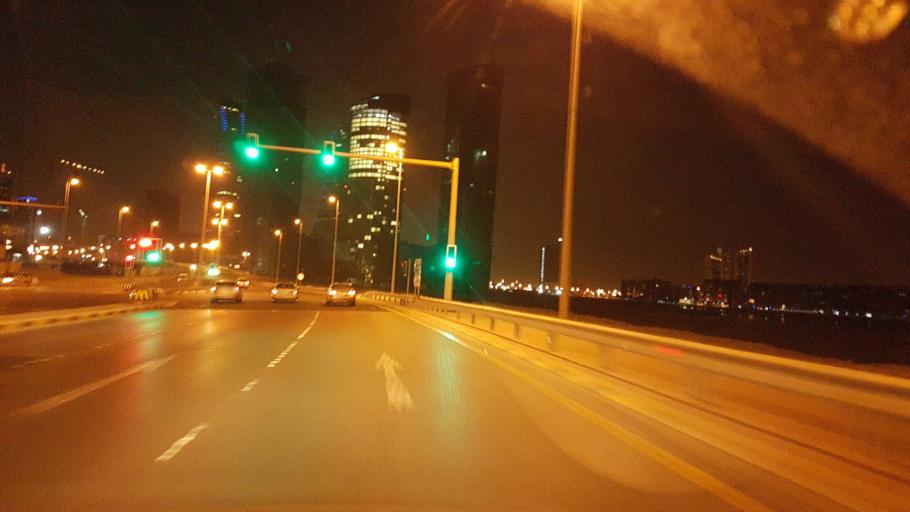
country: BH
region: Manama
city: Manama
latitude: 26.2466
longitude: 50.5744
